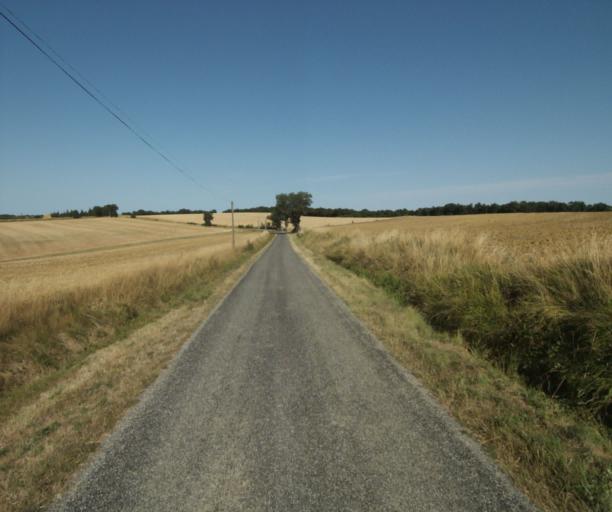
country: FR
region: Midi-Pyrenees
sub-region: Departement de la Haute-Garonne
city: Saint-Felix-Lauragais
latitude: 43.4256
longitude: 1.8420
